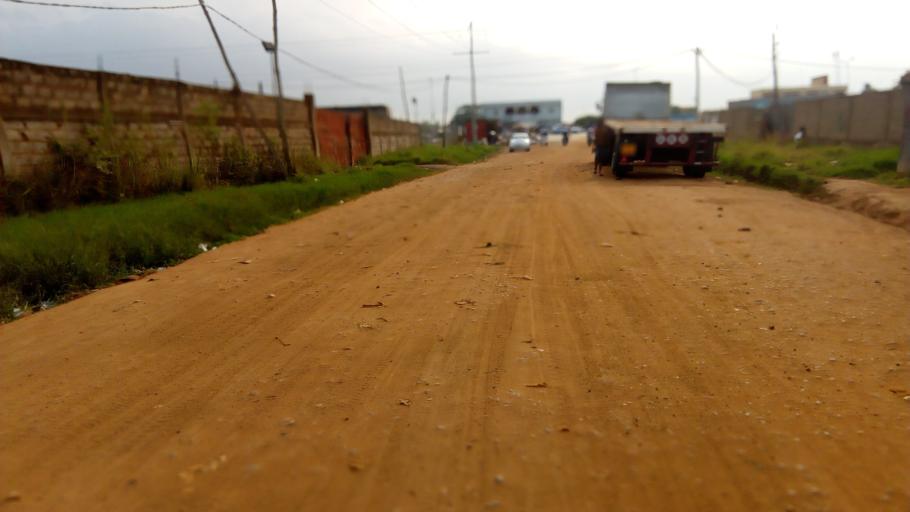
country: TG
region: Maritime
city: Lome
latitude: 6.2517
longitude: 1.2100
